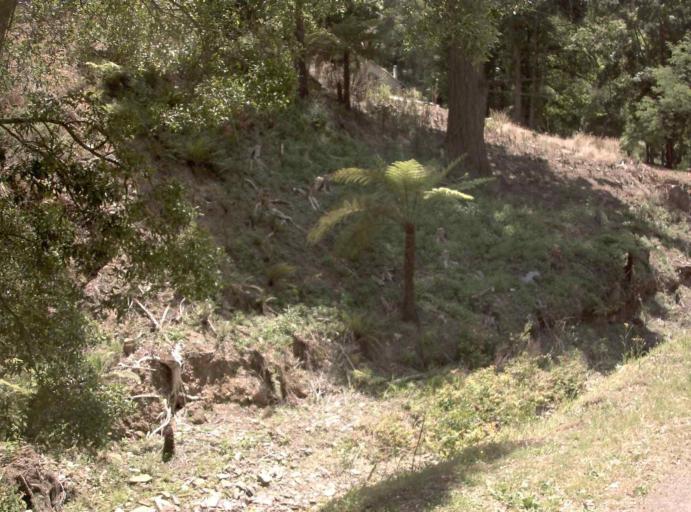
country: AU
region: Victoria
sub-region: Latrobe
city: Traralgon
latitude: -37.9361
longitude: 146.4498
